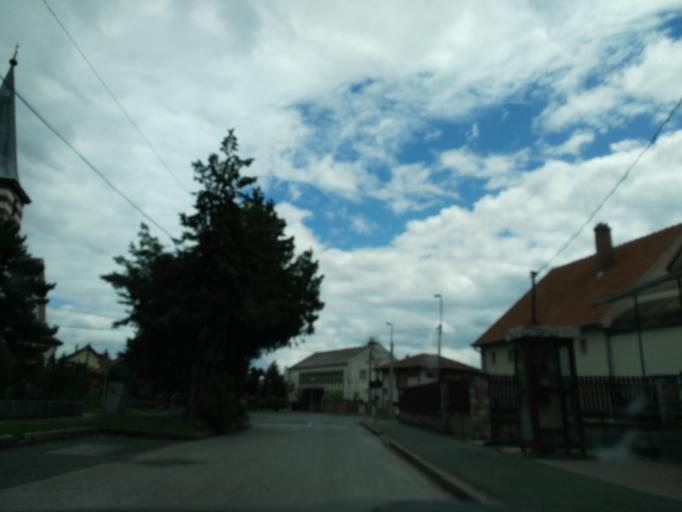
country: HU
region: Hajdu-Bihar
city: Debrecen
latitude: 47.5419
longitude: 21.6535
